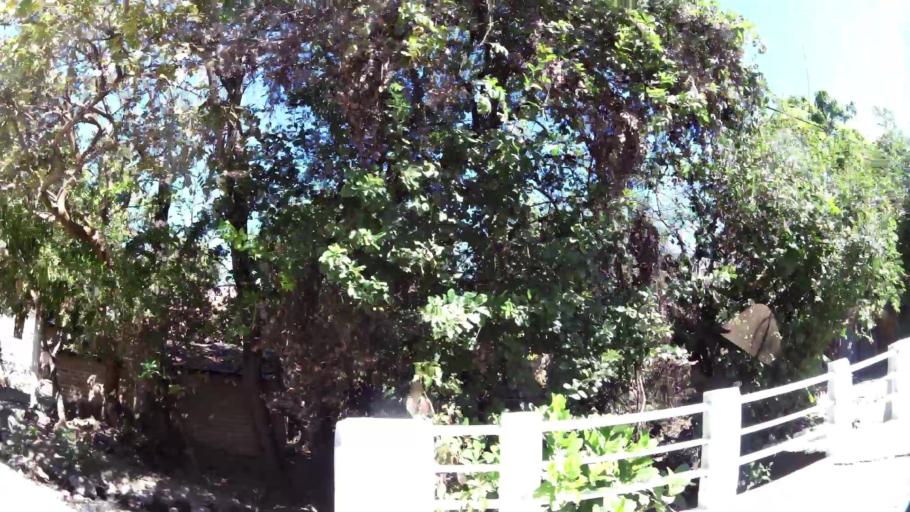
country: SV
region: La Libertad
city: San Juan Opico
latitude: 13.8754
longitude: -89.3550
